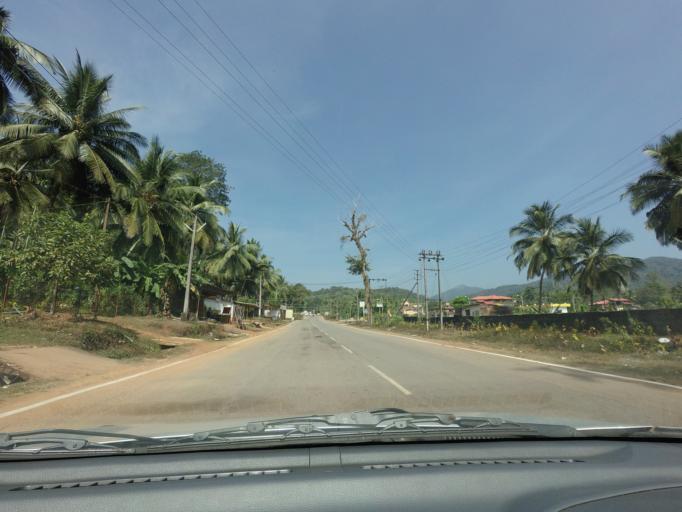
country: IN
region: Karnataka
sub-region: Dakshina Kannada
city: Sulya
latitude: 12.6835
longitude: 75.6091
